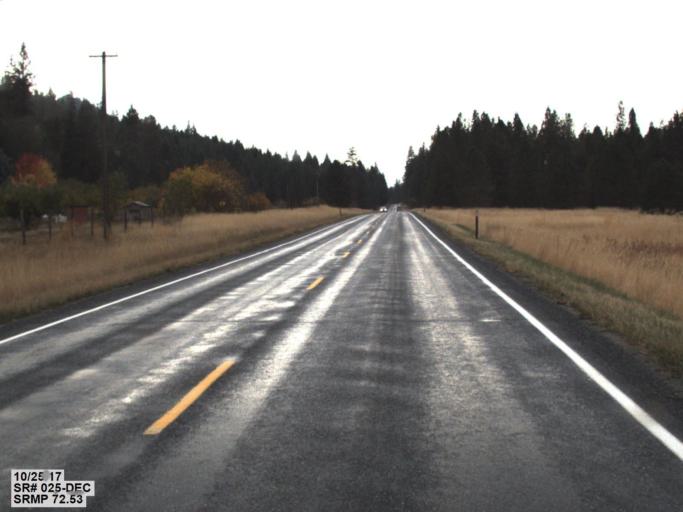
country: US
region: Washington
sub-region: Stevens County
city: Kettle Falls
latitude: 48.5077
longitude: -118.1504
